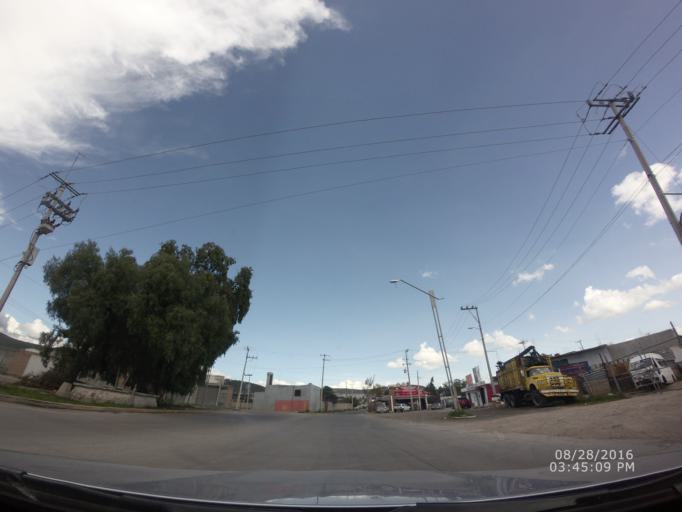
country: MX
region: Hidalgo
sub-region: Mineral de la Reforma
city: PRI Chacon
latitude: 20.0816
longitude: -98.7481
